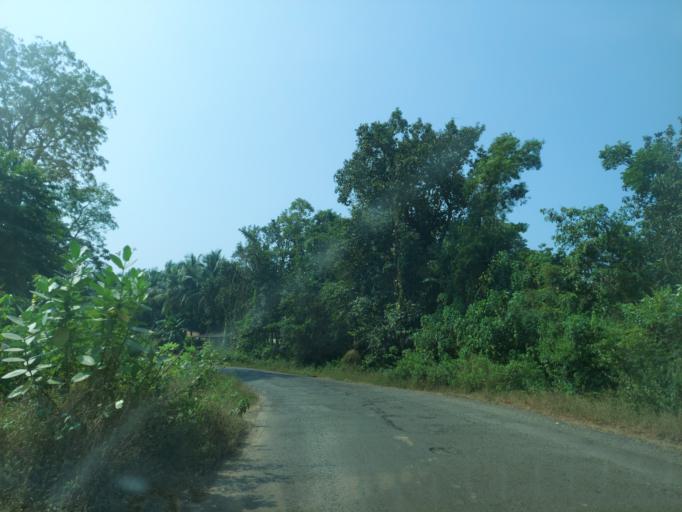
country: IN
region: Maharashtra
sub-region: Sindhudurg
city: Kudal
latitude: 15.9868
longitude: 73.6692
